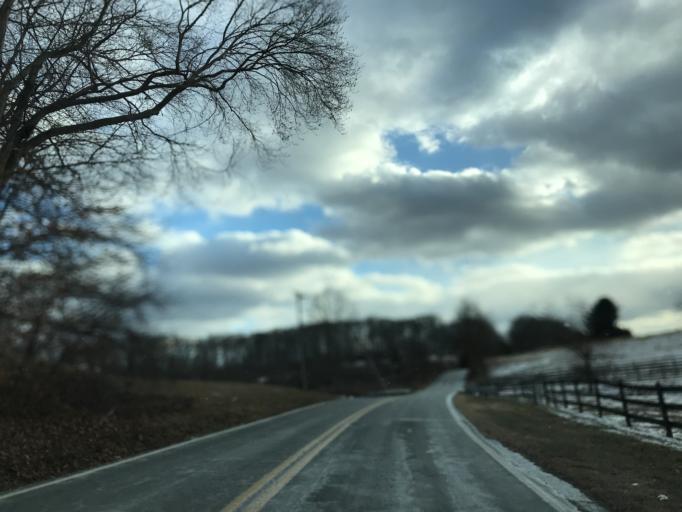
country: US
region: Maryland
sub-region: Harford County
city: Bel Air North
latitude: 39.6227
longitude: -76.3752
